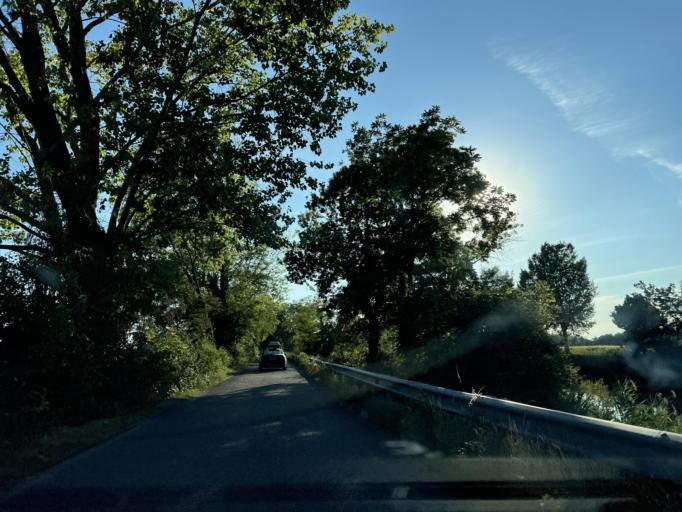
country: IT
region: Friuli Venezia Giulia
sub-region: Provincia di Gorizia
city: Staranzano
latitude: 45.7748
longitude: 13.4946
